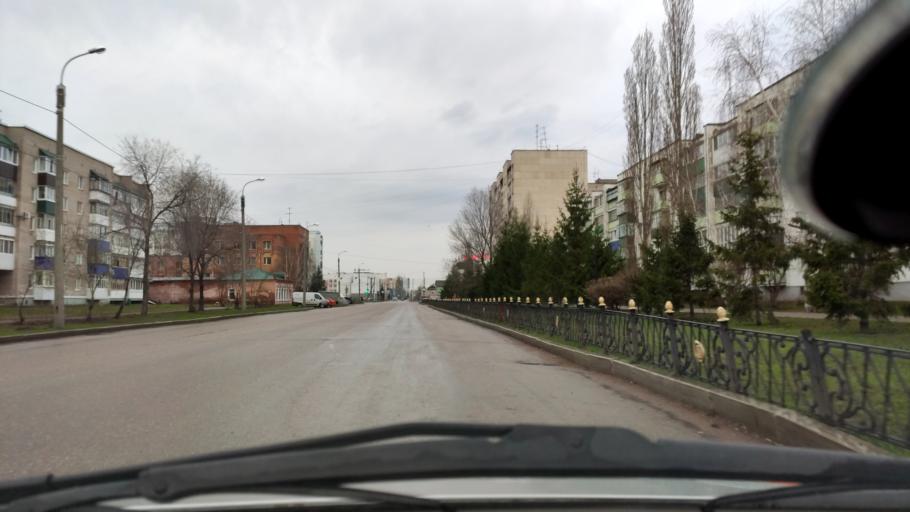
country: RU
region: Bashkortostan
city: Sterlitamak
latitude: 53.6226
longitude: 55.9589
